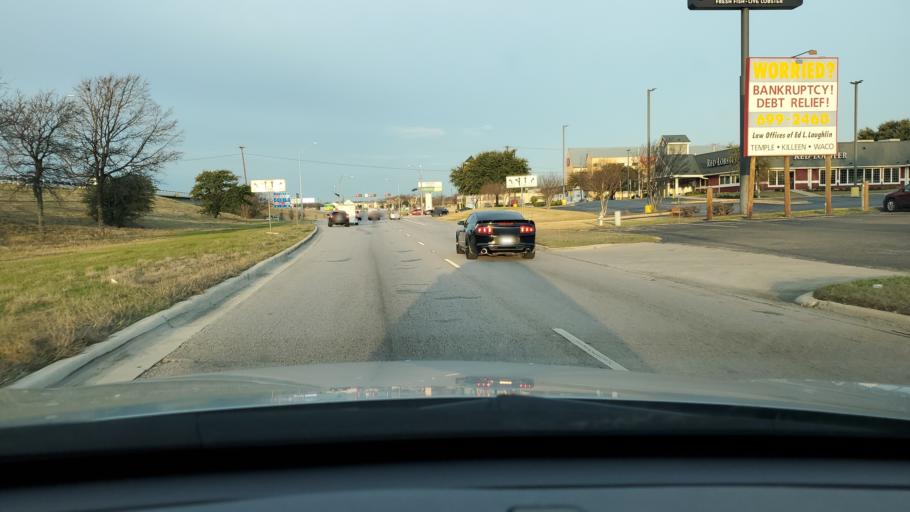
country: US
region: Texas
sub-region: Bell County
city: Killeen
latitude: 31.0948
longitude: -97.7305
